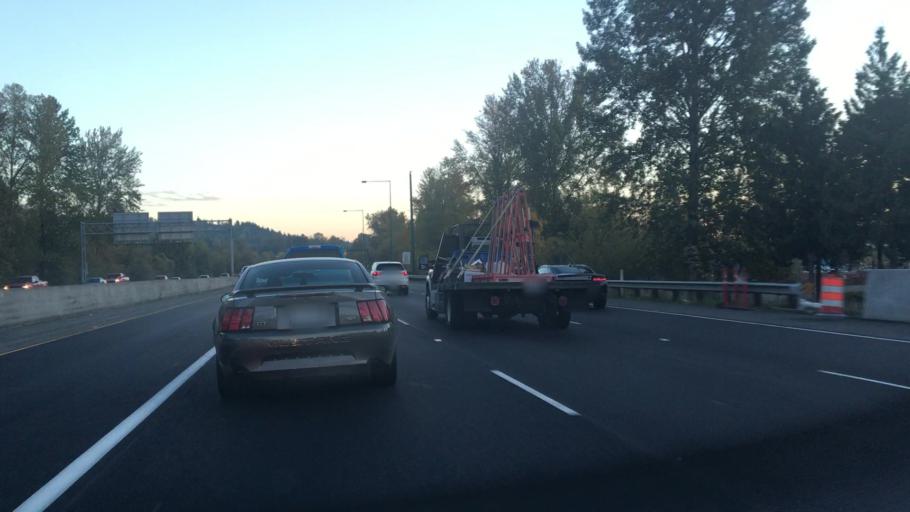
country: US
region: Washington
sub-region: King County
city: Renton
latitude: 47.4560
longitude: -122.2165
